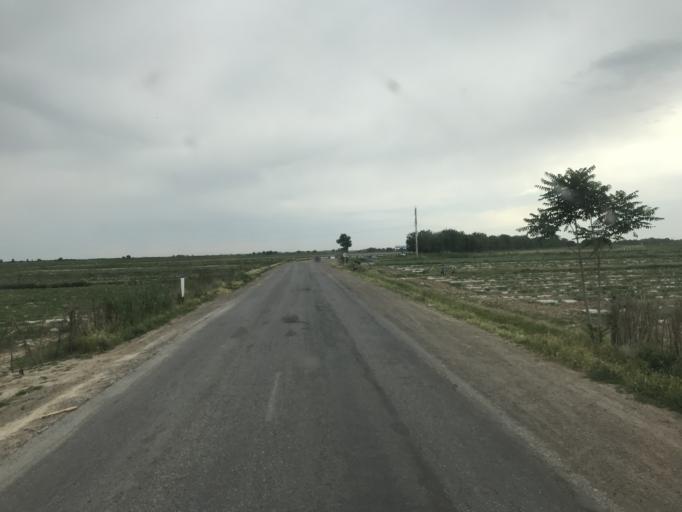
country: KZ
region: Ongtustik Qazaqstan
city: Asykata
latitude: 40.9519
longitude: 68.4564
